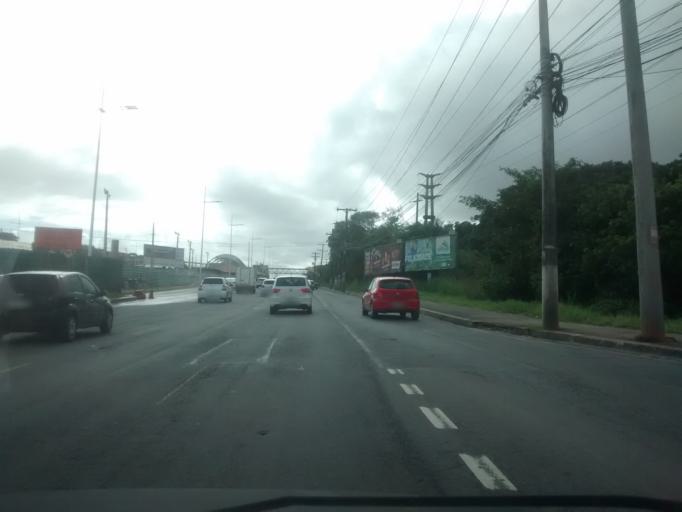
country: BR
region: Bahia
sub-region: Salvador
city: Salvador
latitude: -12.9593
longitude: -38.4312
